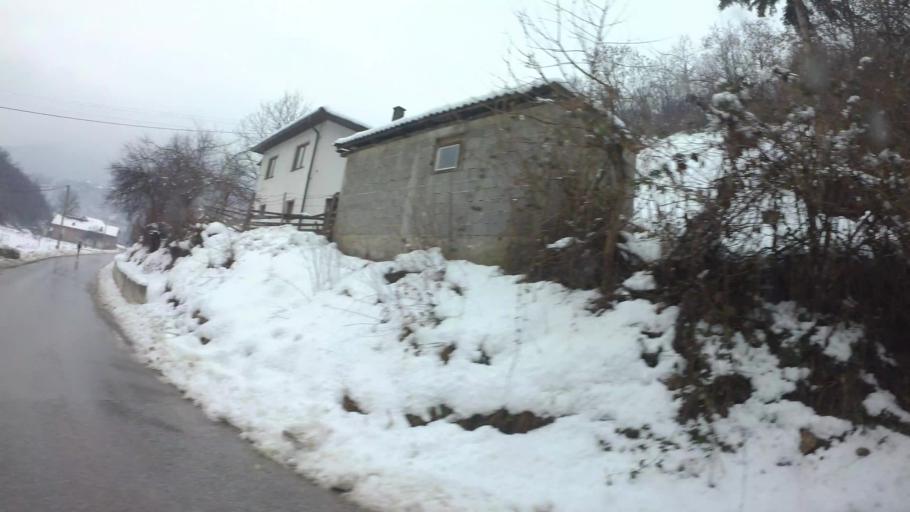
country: BA
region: Federation of Bosnia and Herzegovina
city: Hadzici
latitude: 43.8435
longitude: 18.2593
